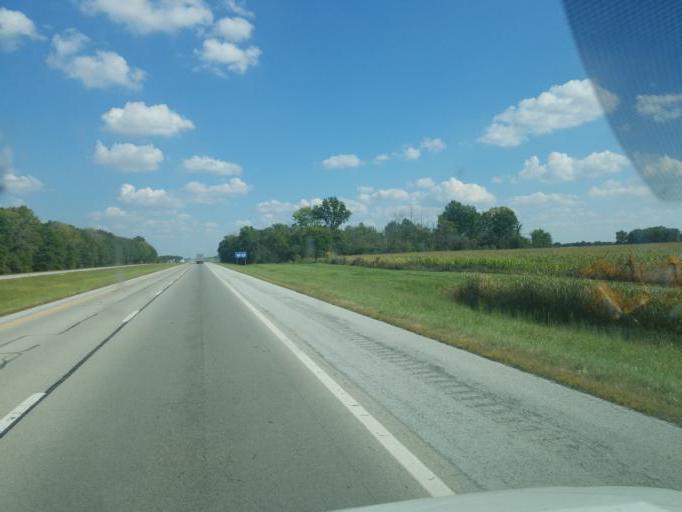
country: US
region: Ohio
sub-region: Allen County
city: Lima
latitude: 40.8240
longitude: -84.1115
